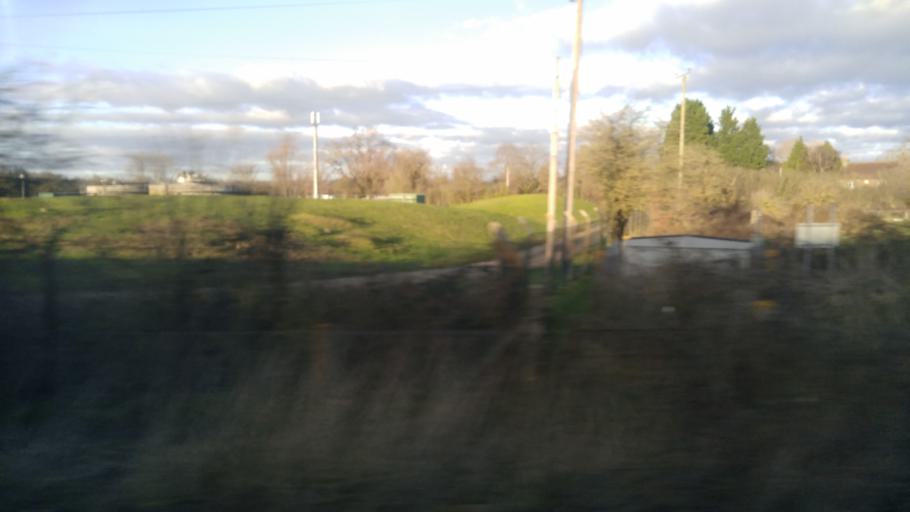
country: GB
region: England
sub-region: Kent
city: Staplehurst
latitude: 51.1710
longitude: 0.5586
